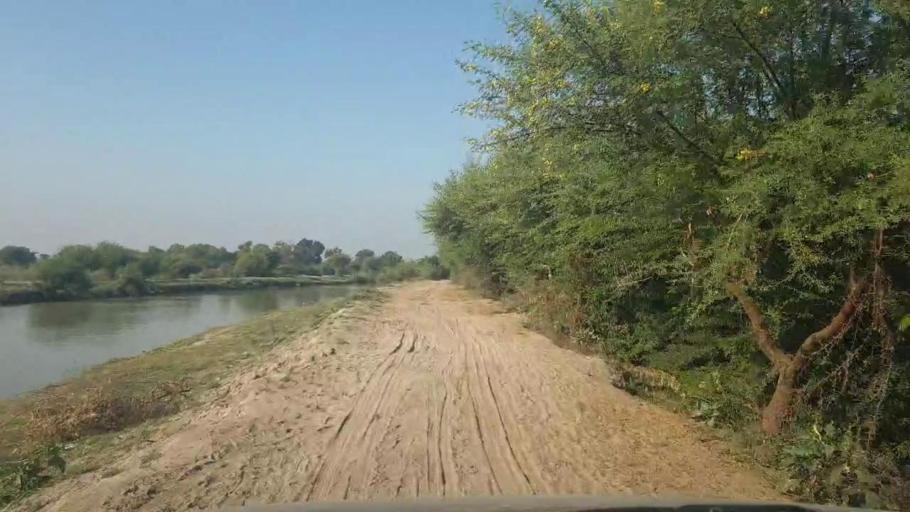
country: PK
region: Sindh
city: Badin
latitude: 24.7134
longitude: 68.8997
